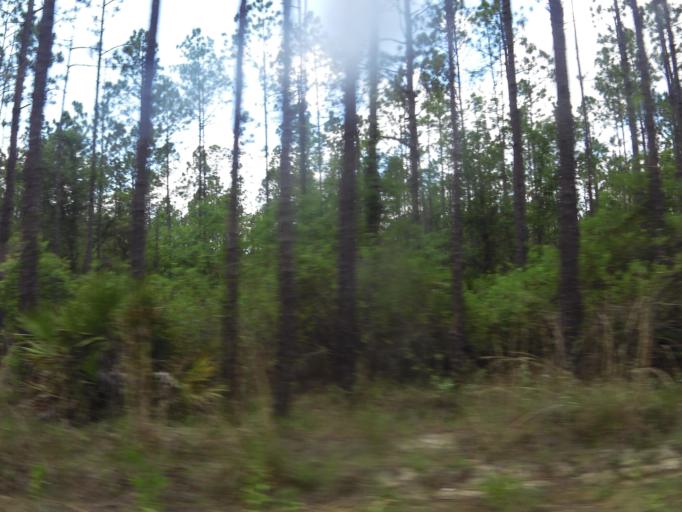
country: US
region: Florida
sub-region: Clay County
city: Asbury Lake
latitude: 29.8874
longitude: -81.8522
